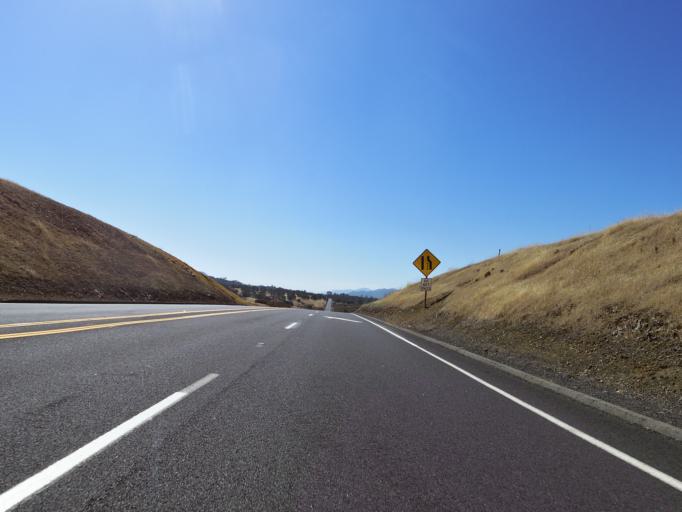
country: US
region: California
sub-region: Tuolumne County
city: Tuolumne City
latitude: 37.7091
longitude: -120.3111
